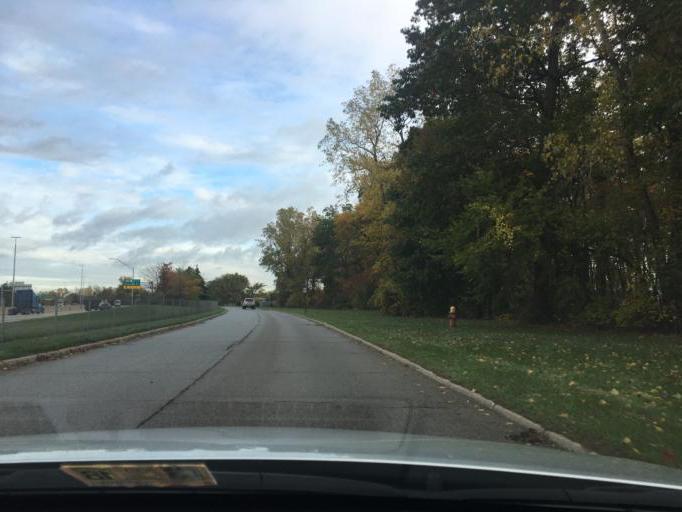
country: US
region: Michigan
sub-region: Wayne County
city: Melvindale
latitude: 42.2911
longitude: -83.2053
